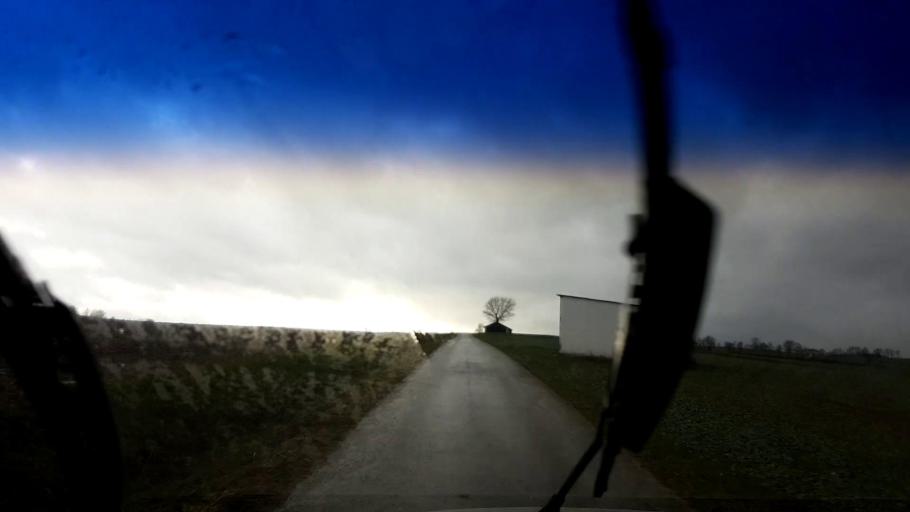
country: DE
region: Bavaria
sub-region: Upper Franconia
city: Memmelsdorf
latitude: 49.9700
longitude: 10.9789
